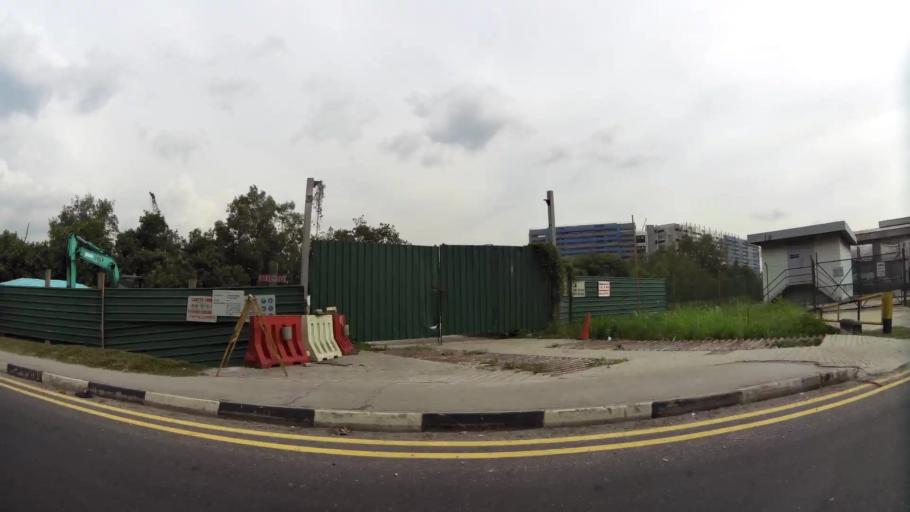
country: MY
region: Johor
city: Johor Bahru
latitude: 1.4343
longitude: 103.7520
